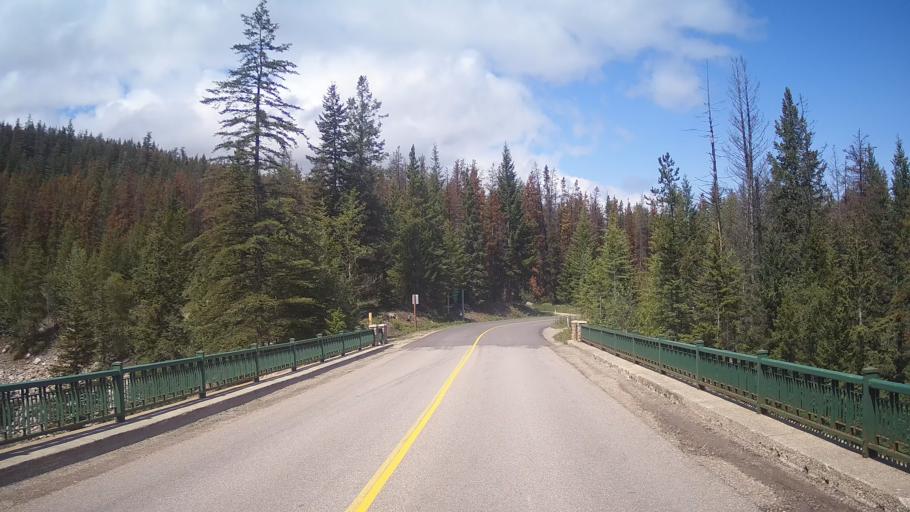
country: CA
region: Alberta
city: Jasper Park Lodge
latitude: 52.7741
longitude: -118.0317
